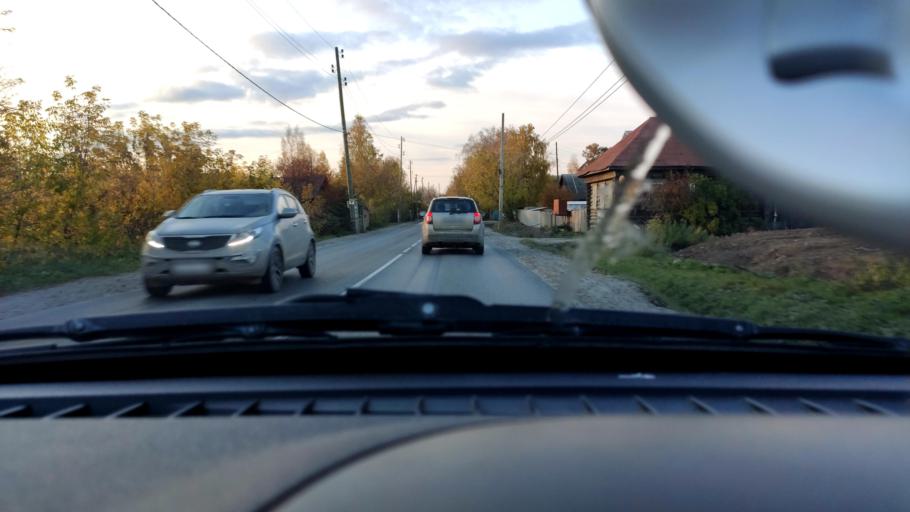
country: RU
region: Perm
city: Kondratovo
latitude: 57.9618
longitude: 56.1321
